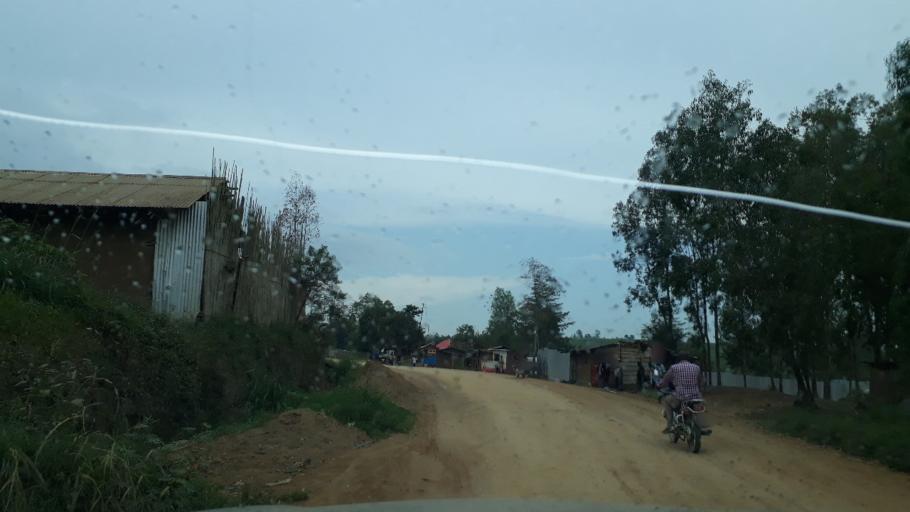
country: CD
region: Eastern Province
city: Bunia
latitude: 1.5805
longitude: 30.2504
